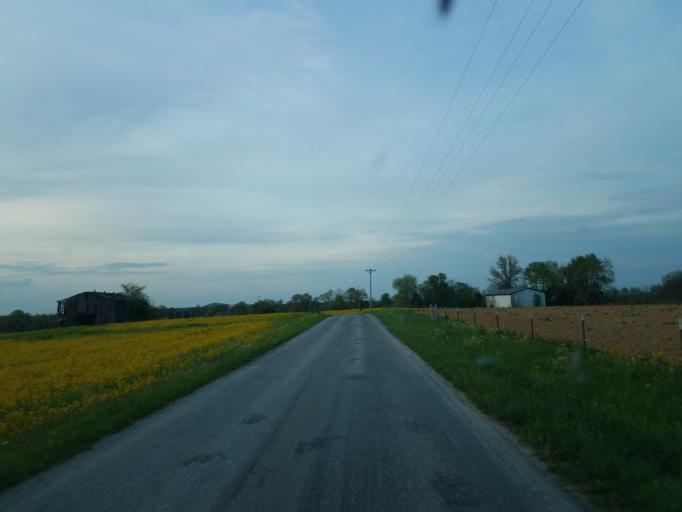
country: US
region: Kentucky
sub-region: Green County
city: Greensburg
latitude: 37.1928
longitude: -85.6898
